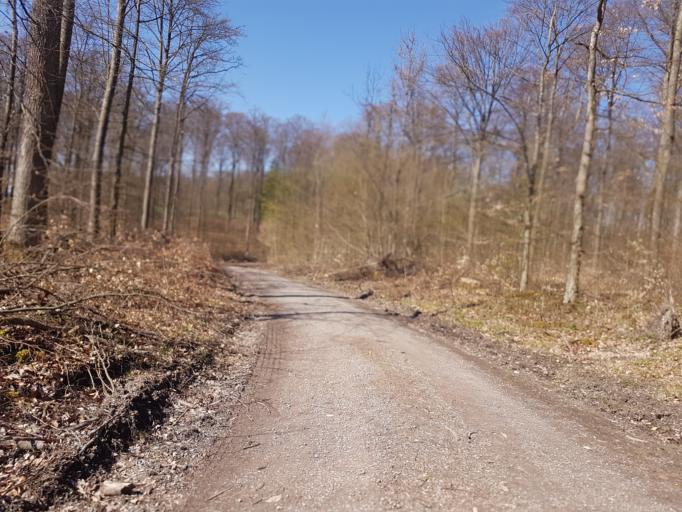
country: DE
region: Baden-Wuerttemberg
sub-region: Regierungsbezirk Stuttgart
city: Jagsthausen
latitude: 49.3409
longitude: 9.4879
